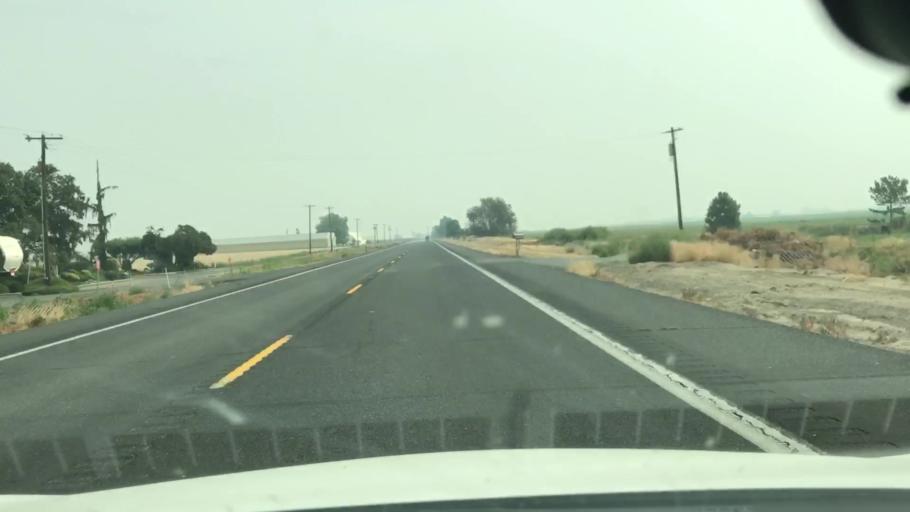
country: US
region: Washington
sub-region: Grant County
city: Quincy
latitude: 47.2343
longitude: -119.7578
